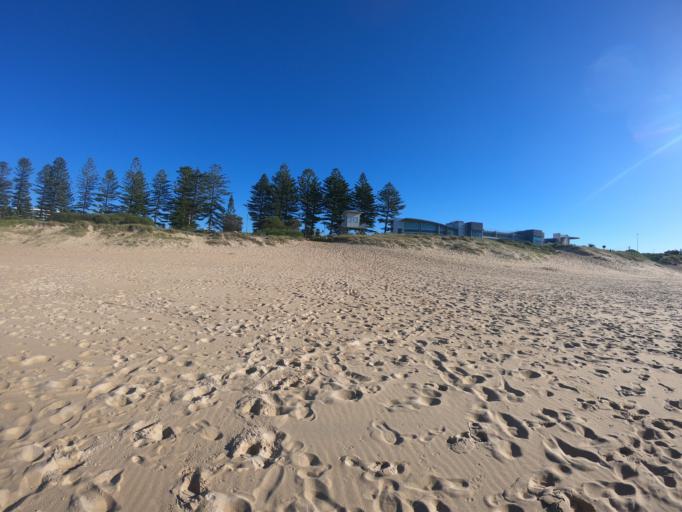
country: AU
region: New South Wales
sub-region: Wollongong
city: Wollongong
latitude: -34.4241
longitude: 150.9064
